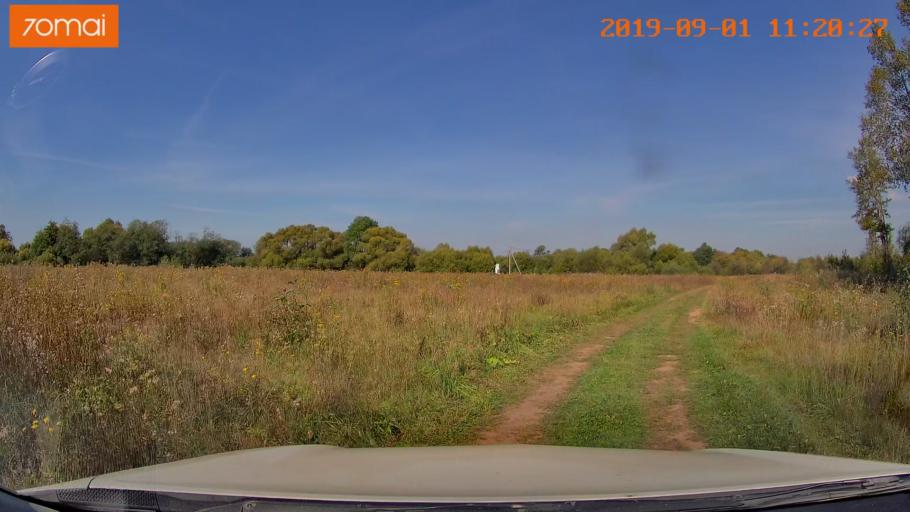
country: RU
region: Kaluga
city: Detchino
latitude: 54.8293
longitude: 36.3611
